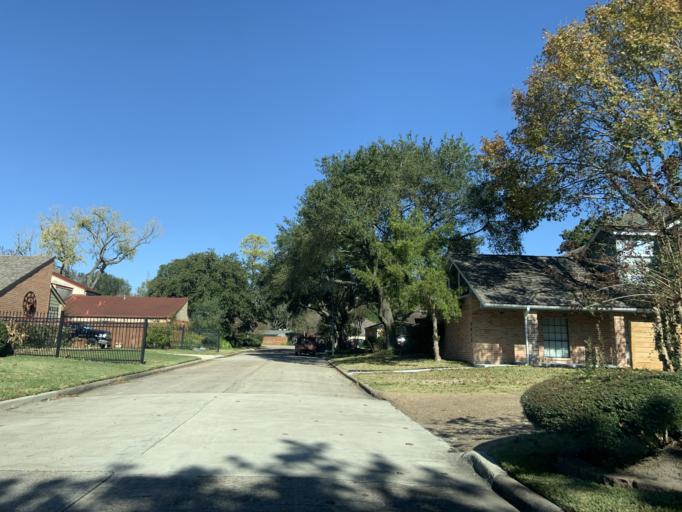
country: US
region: Texas
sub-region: Harris County
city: Bellaire
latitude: 29.6775
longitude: -95.5134
